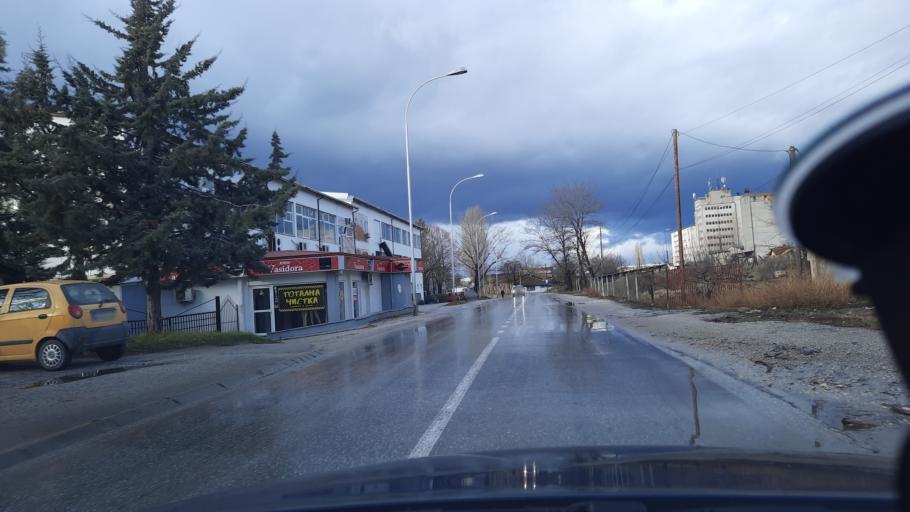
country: MK
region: Prilep
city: Markov Grad
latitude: 41.3437
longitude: 21.5372
